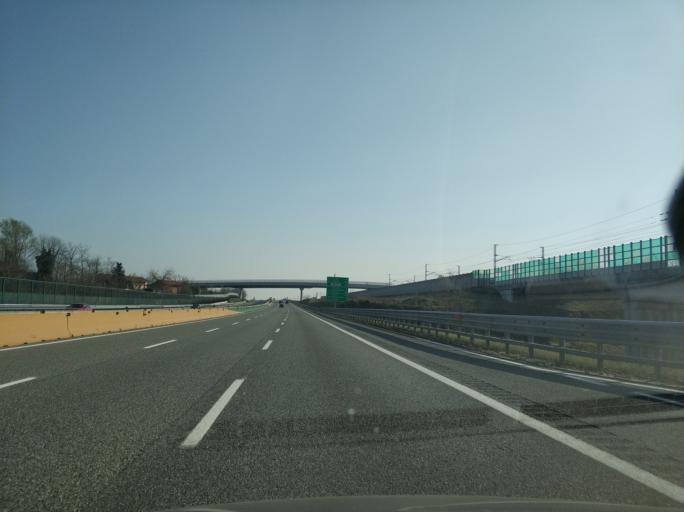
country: IT
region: Piedmont
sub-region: Provincia di Vercelli
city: Saluggia
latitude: 45.2502
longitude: 7.9917
